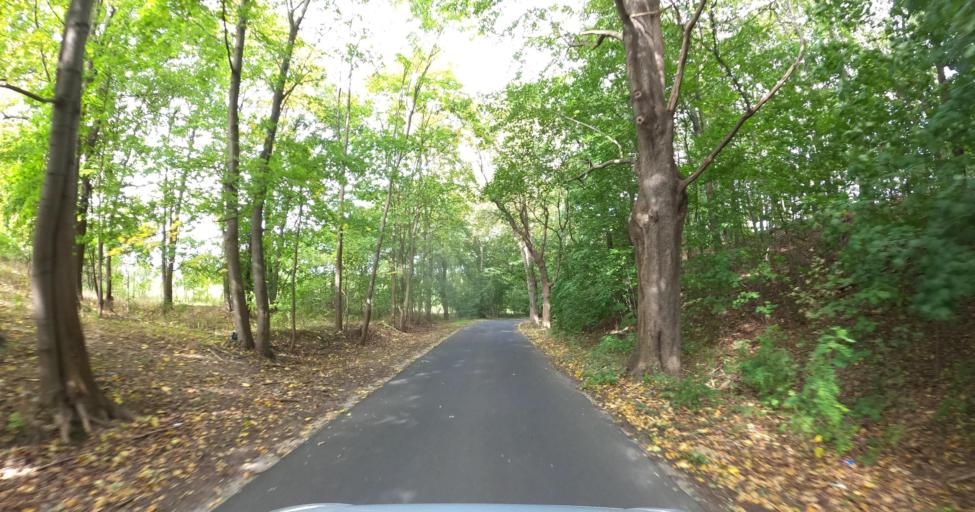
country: PL
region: Lubusz
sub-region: Powiat zielonogorski
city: Zabor
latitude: 51.9556
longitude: 15.6892
